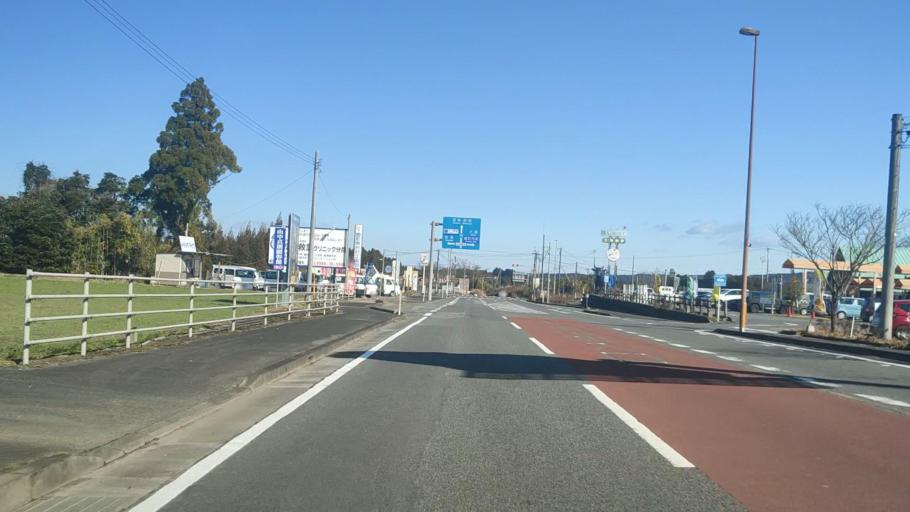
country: JP
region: Kagoshima
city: Sueyoshicho-ninokata
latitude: 31.6880
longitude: 130.9693
